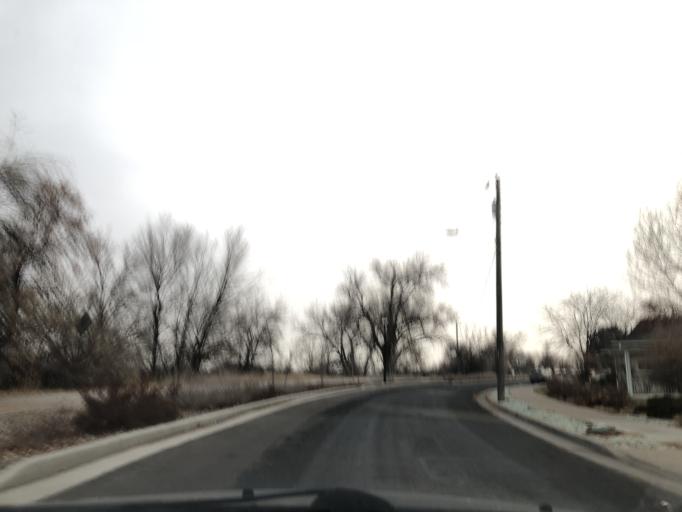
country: US
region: Utah
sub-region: Cache County
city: Logan
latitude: 41.7375
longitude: -111.8197
